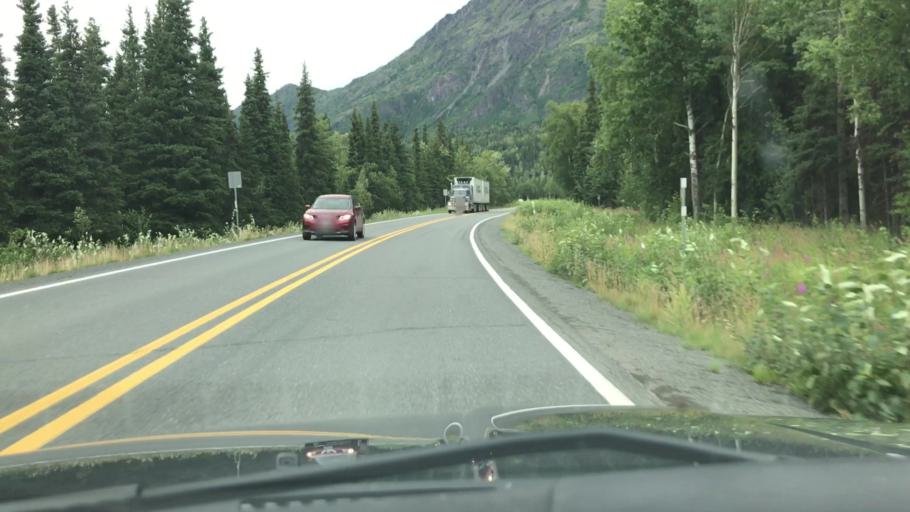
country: US
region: Alaska
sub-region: Kenai Peninsula Borough
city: Seward
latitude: 60.4841
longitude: -149.9591
